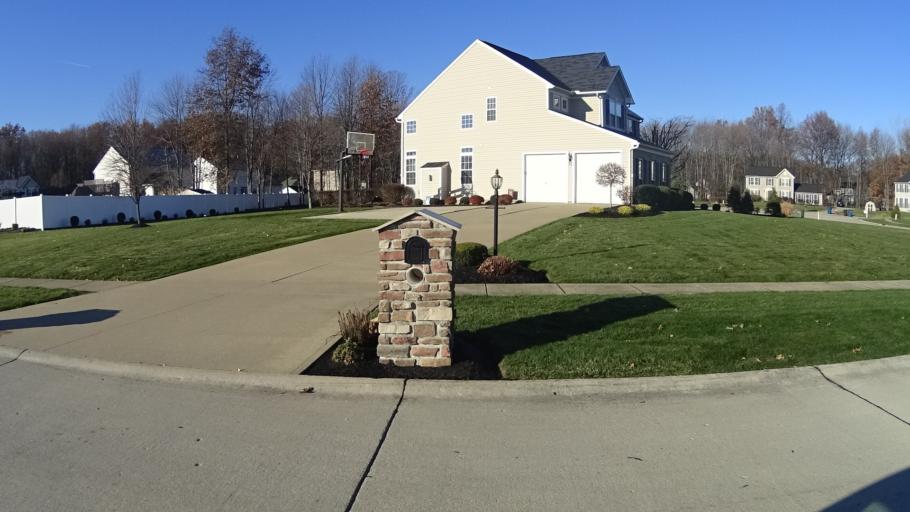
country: US
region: Ohio
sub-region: Lorain County
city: Sheffield Lake
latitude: 41.4565
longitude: -82.0820
